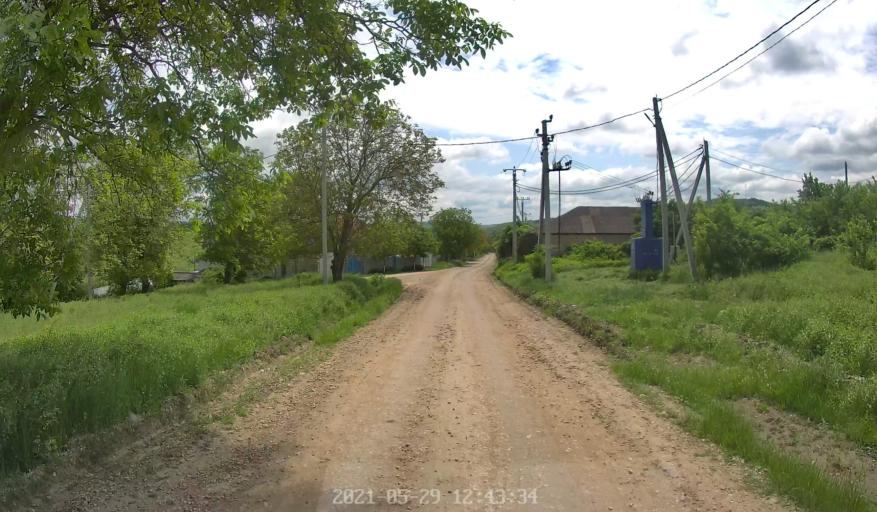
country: MD
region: Hincesti
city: Hincesti
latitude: 46.8738
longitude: 28.6357
